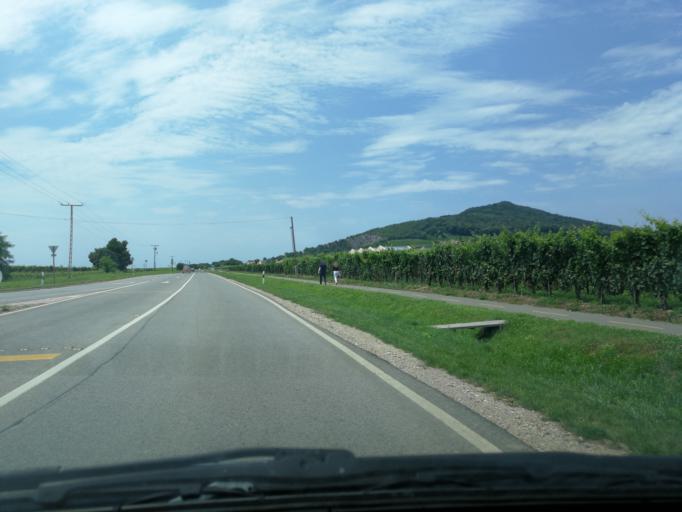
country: HU
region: Baranya
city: Villany
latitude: 45.8611
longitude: 18.4417
